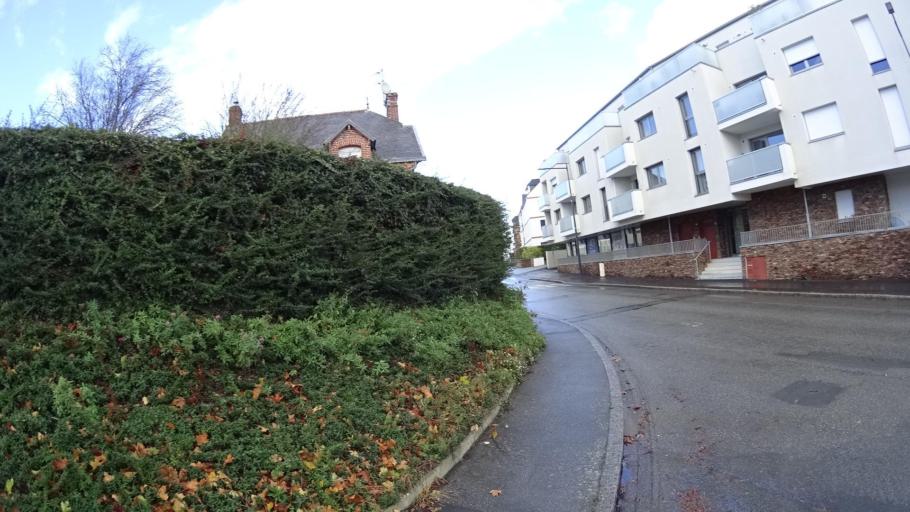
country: FR
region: Brittany
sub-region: Departement d'Ille-et-Vilaine
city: Chatillon-sur-Seiche
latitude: 48.0377
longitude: -1.6722
